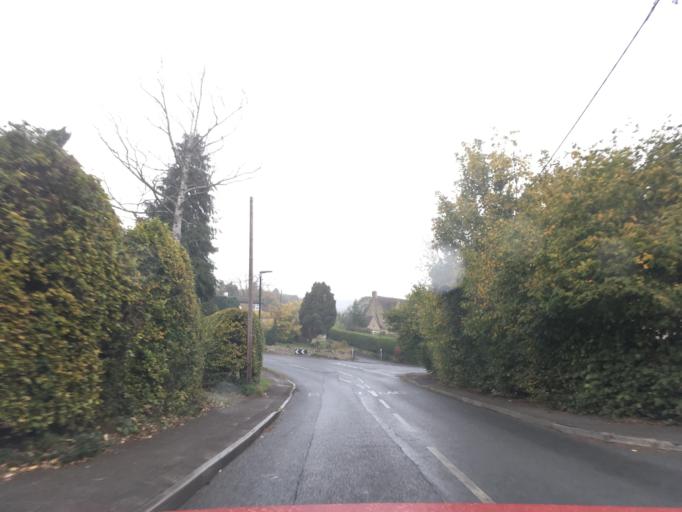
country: GB
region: England
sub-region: Gloucestershire
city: Stonehouse
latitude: 51.7523
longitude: -2.2486
